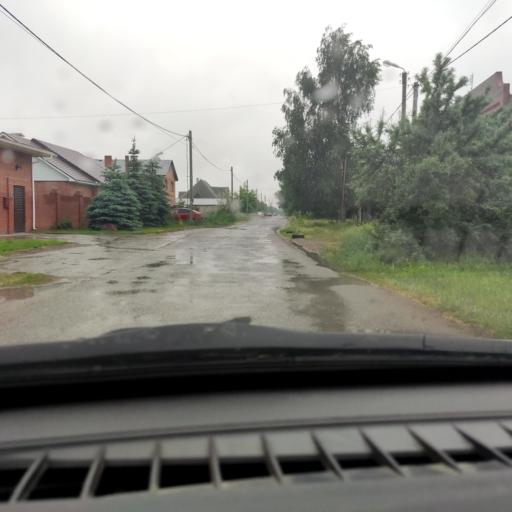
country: RU
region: Samara
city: Tol'yatti
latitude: 53.5647
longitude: 49.3814
